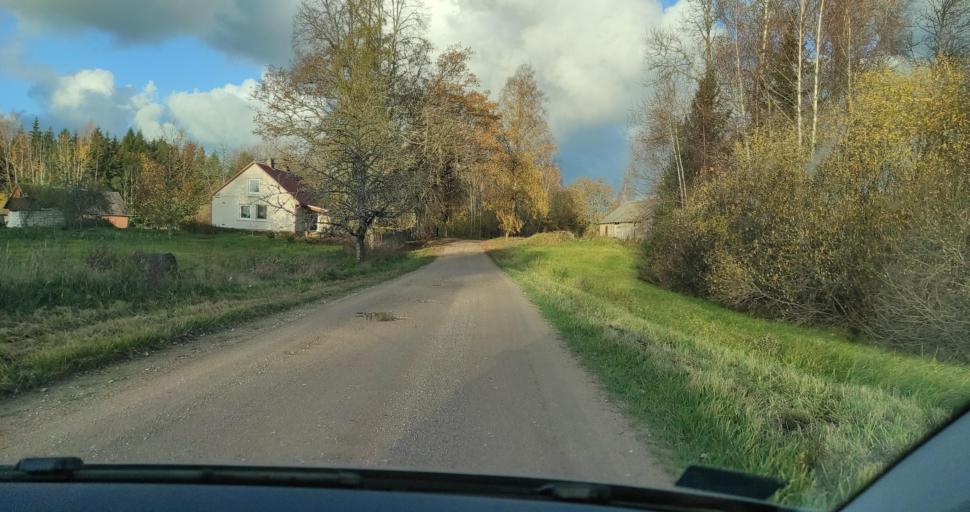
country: LV
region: Alsunga
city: Alsunga
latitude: 56.9495
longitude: 21.6314
